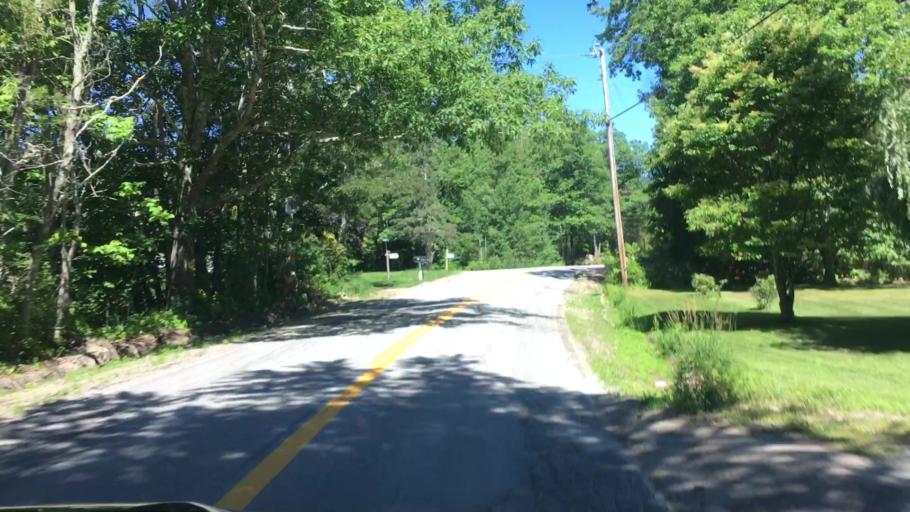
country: US
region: Maine
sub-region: Hancock County
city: Penobscot
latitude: 44.4275
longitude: -68.7125
